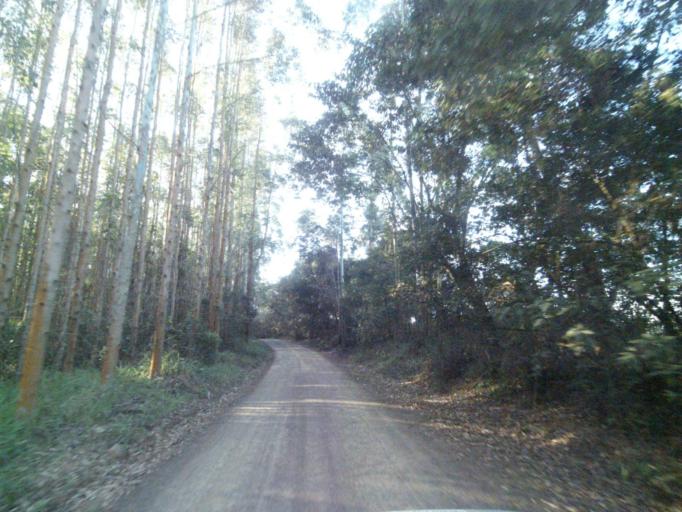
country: BR
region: Parana
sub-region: Telemaco Borba
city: Telemaco Borba
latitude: -24.5026
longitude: -50.5980
